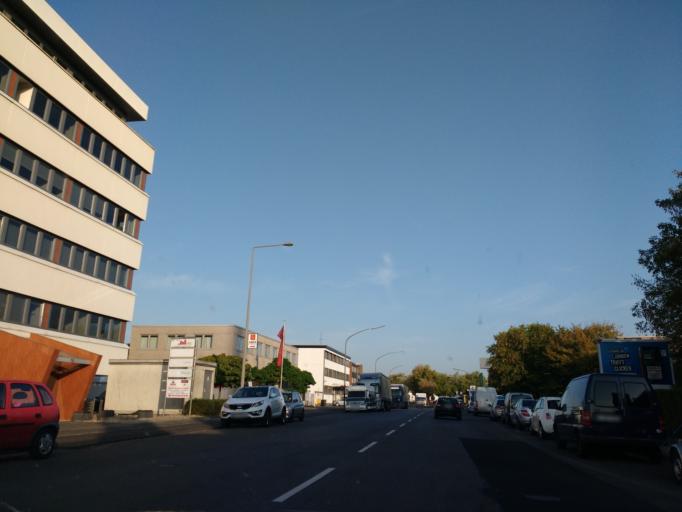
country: DE
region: North Rhine-Westphalia
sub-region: Regierungsbezirk Koln
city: Bilderstoeckchen
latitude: 50.9805
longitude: 6.9185
